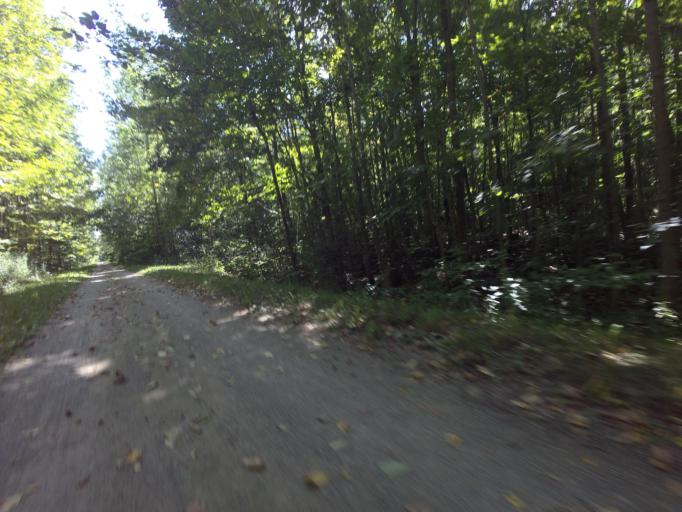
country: CA
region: Ontario
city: Orangeville
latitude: 43.7938
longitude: -80.3067
